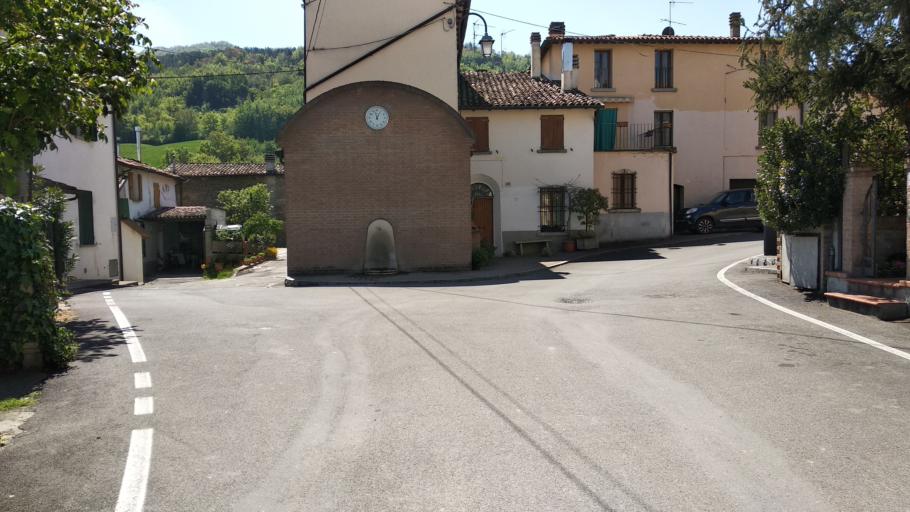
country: IT
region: Emilia-Romagna
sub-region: Provincia di Ravenna
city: Riolo Terme
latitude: 44.2612
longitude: 11.6722
